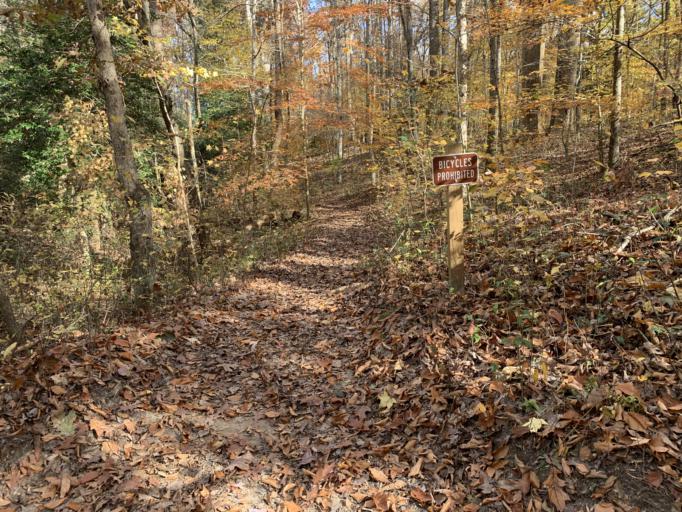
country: US
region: Delaware
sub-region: Kent County
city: Felton
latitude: 38.9789
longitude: -75.5443
